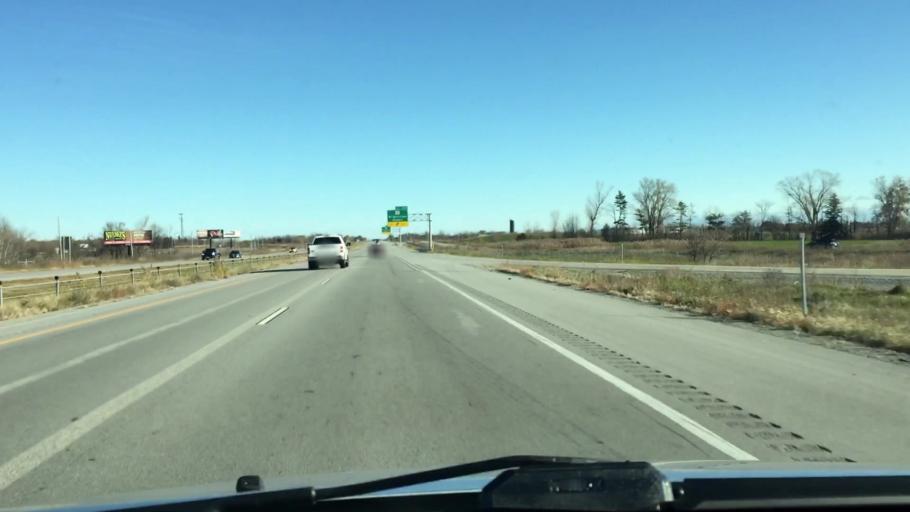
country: US
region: Wisconsin
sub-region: Brown County
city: Wrightstown
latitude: 44.3420
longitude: -88.1999
